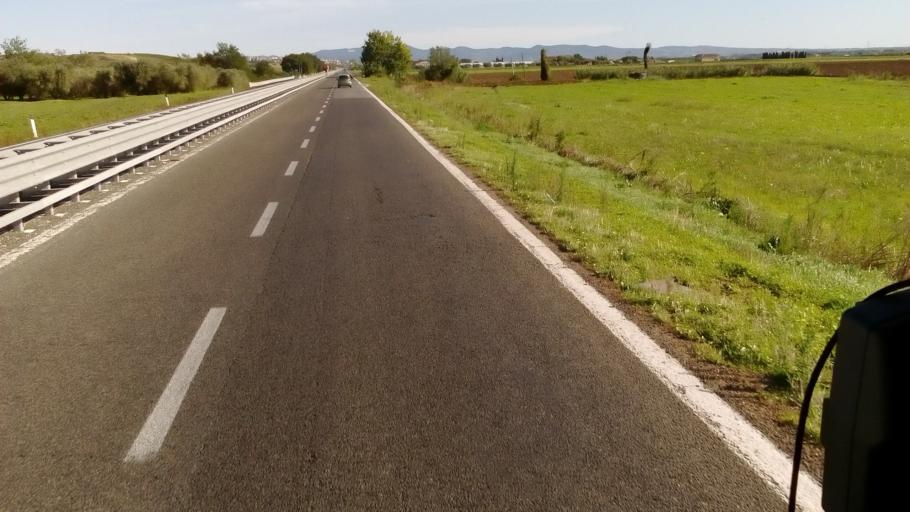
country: IT
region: Latium
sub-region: Provincia di Viterbo
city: Tarquinia
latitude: 42.2796
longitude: 11.6979
